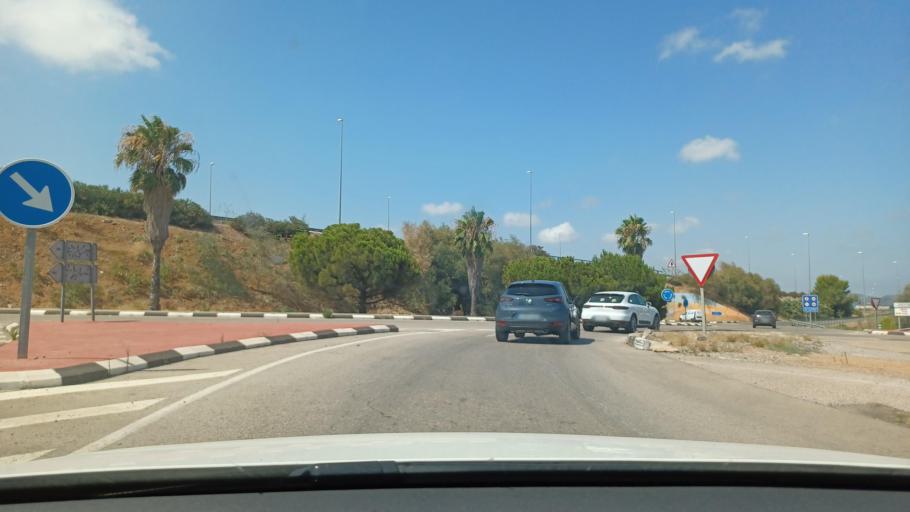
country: ES
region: Valencia
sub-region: Provincia de Valencia
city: Faura
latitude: 39.7034
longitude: -0.2607
